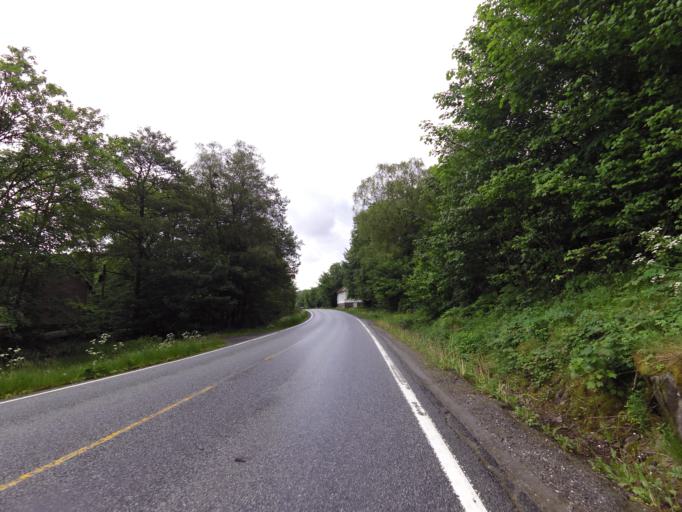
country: NO
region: Vest-Agder
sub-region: Farsund
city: Farsund
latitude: 58.1008
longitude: 6.8652
